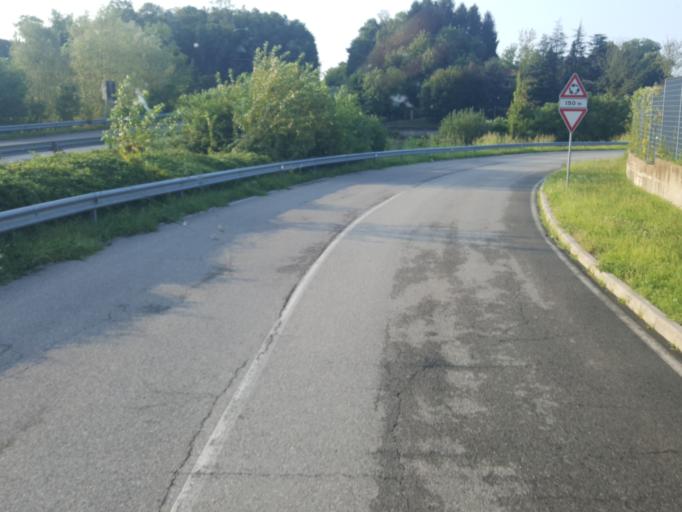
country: IT
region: Lombardy
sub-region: Provincia di Varese
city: Gemonio
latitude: 45.8827
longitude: 8.6675
